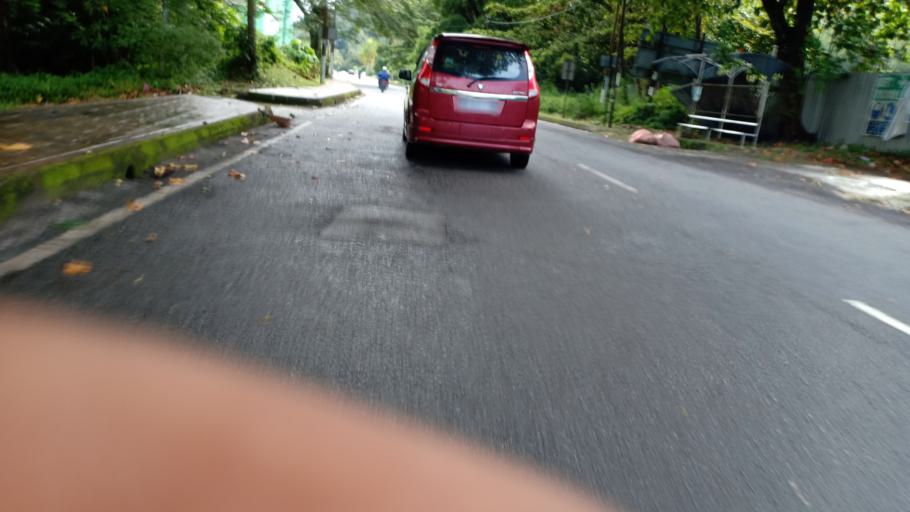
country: MY
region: Penang
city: Tanjung Tokong
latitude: 5.4598
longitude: 100.2178
